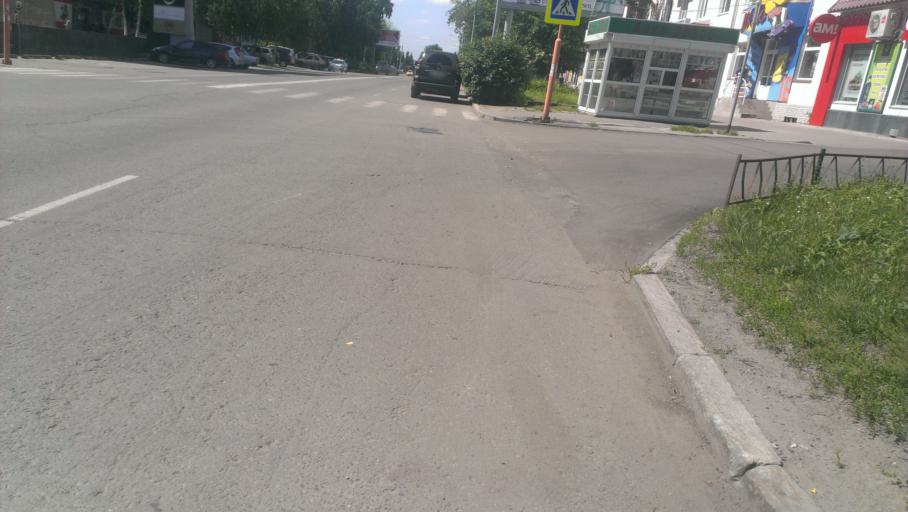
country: RU
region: Altai Krai
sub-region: Gorod Barnaulskiy
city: Barnaul
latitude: 53.3489
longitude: 83.7662
